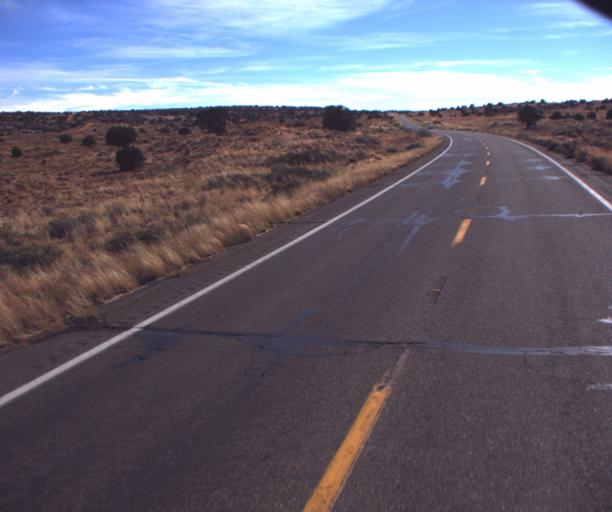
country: US
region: Arizona
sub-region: Coconino County
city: Kaibito
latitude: 36.5815
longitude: -111.1443
